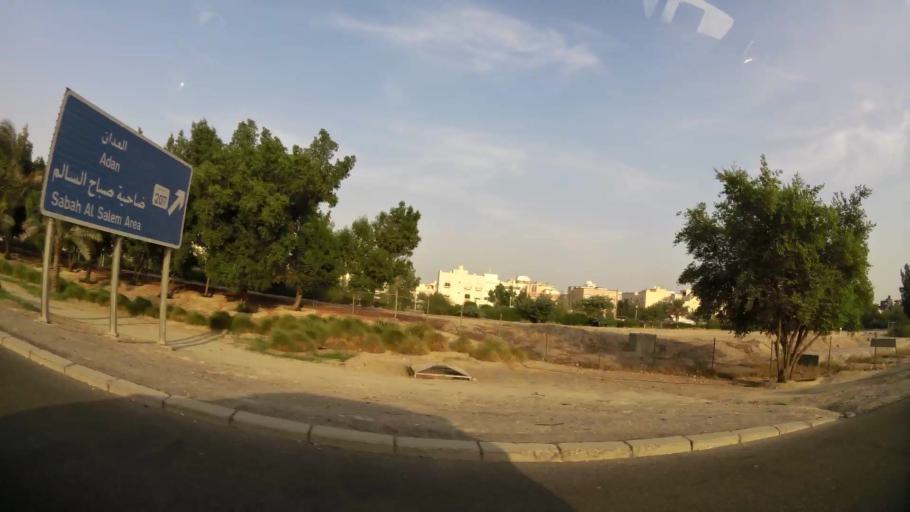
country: KW
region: Mubarak al Kabir
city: Sabah as Salim
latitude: 29.2349
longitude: 48.0515
